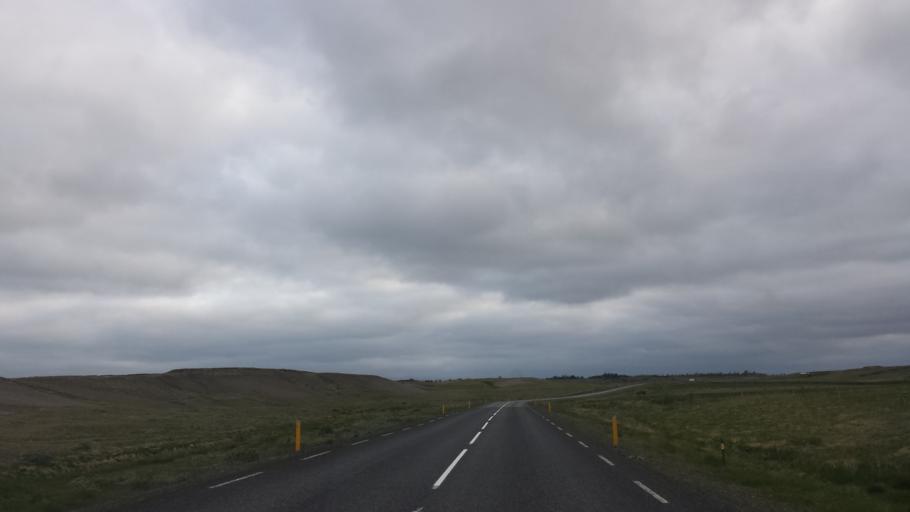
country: IS
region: South
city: Selfoss
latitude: 64.1260
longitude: -20.5927
